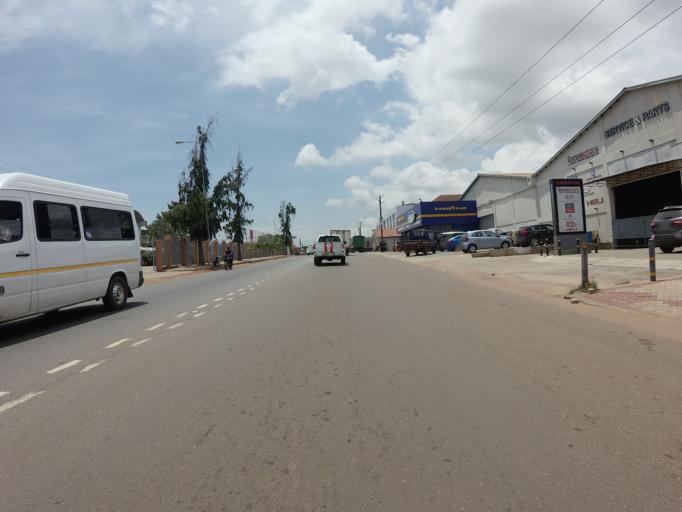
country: GH
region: Greater Accra
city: Medina Estates
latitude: 5.6358
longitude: -0.1313
